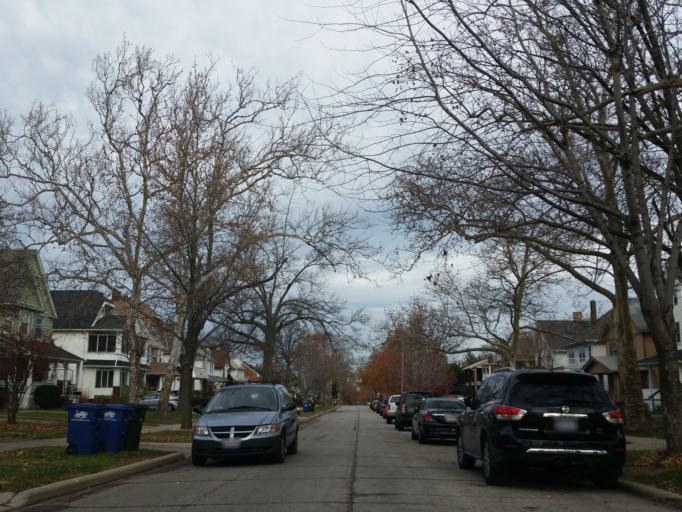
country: US
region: Ohio
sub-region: Cuyahoga County
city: Lakewood
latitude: 41.4790
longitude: -81.7791
